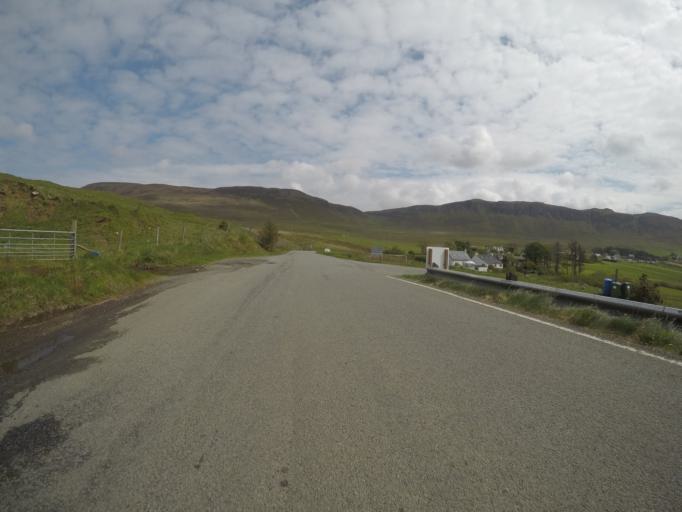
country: GB
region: Scotland
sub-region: Highland
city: Portree
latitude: 57.6217
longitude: -6.3768
